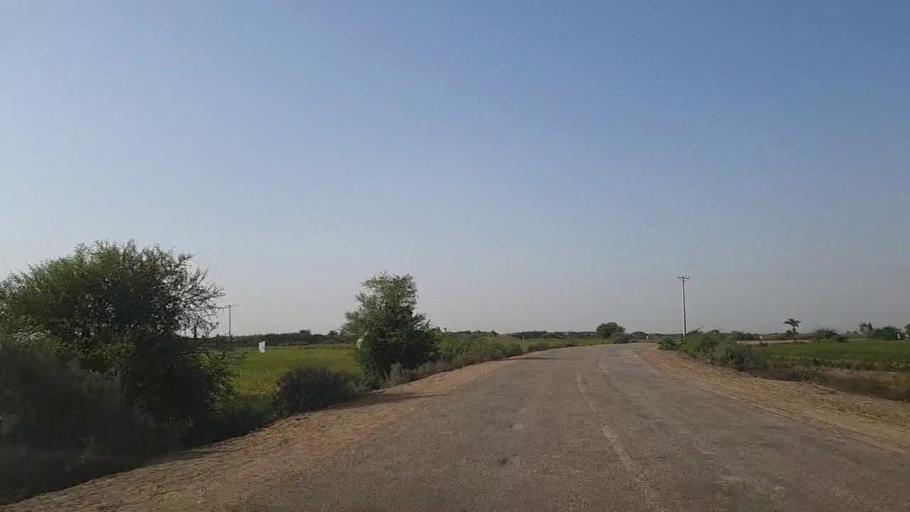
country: PK
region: Sindh
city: Mirpur Batoro
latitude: 24.5820
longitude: 68.3969
